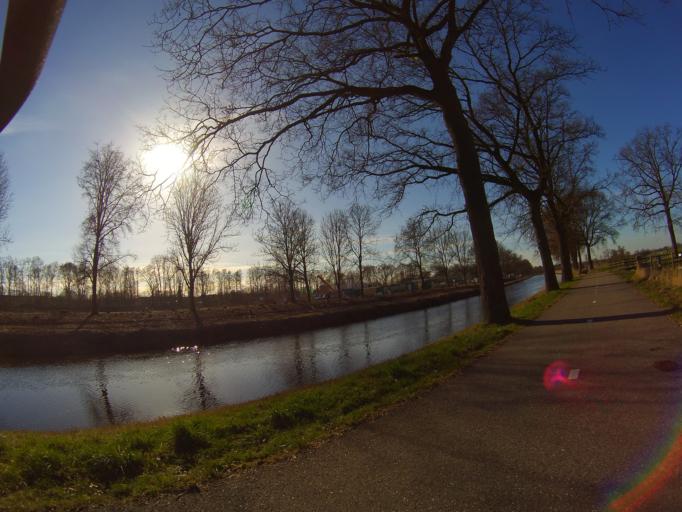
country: NL
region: Utrecht
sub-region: Gemeente Leusden
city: Leusden
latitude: 52.1407
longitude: 5.4469
